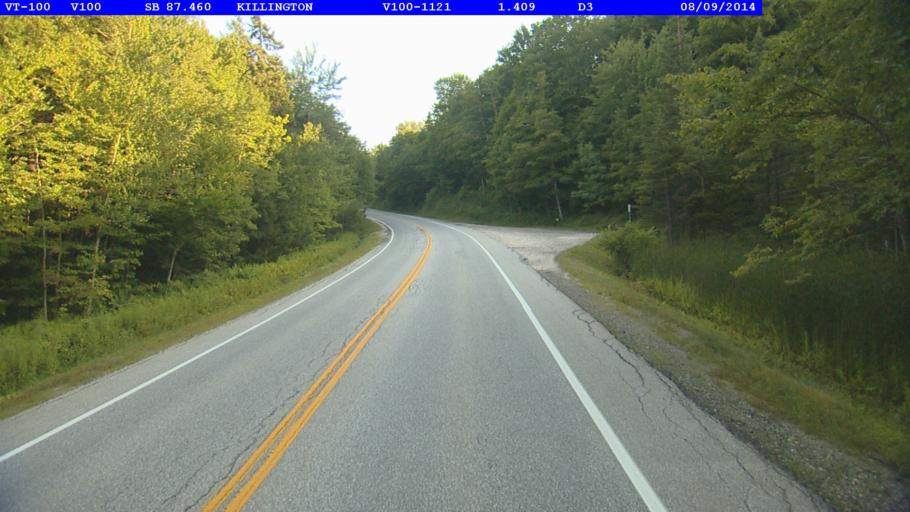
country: US
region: Vermont
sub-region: Rutland County
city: Rutland
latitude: 43.6863
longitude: -72.8136
